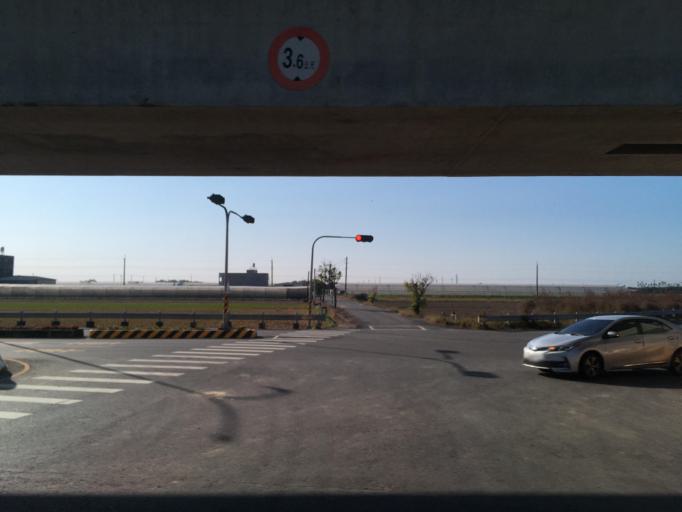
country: TW
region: Taiwan
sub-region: Chiayi
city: Taibao
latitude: 23.4399
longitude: 120.3230
